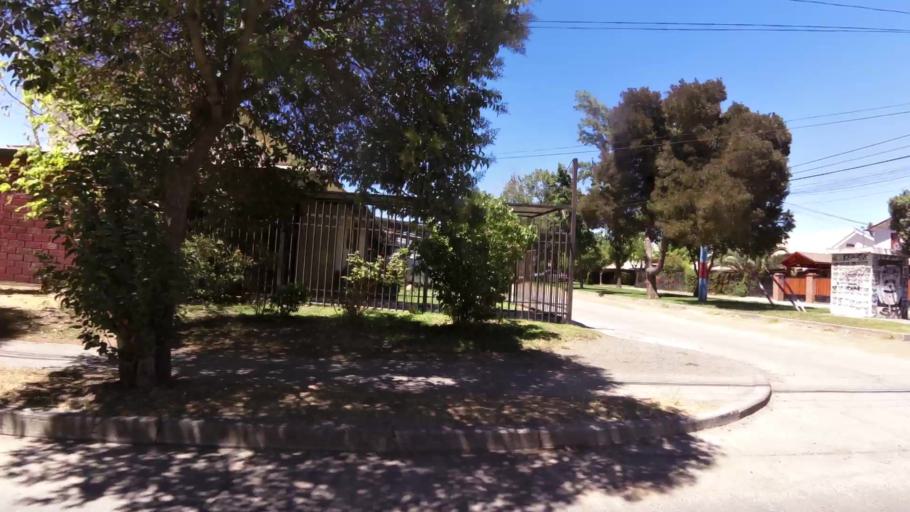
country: CL
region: O'Higgins
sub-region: Provincia de Cachapoal
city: Rancagua
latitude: -34.1577
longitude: -70.7064
